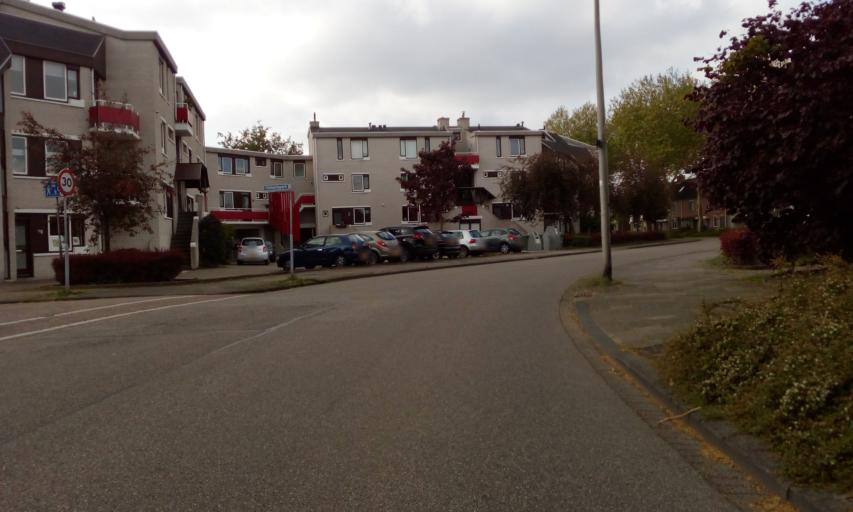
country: NL
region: South Holland
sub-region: Gemeente Zoetermeer
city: Zoetermeer
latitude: 52.0676
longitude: 4.5083
